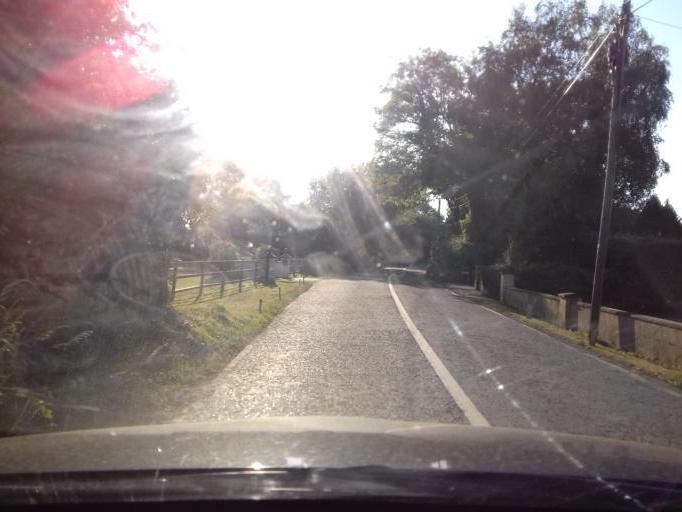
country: IE
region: Leinster
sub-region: An Mhi
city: Ashbourne
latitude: 53.5527
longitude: -6.3788
